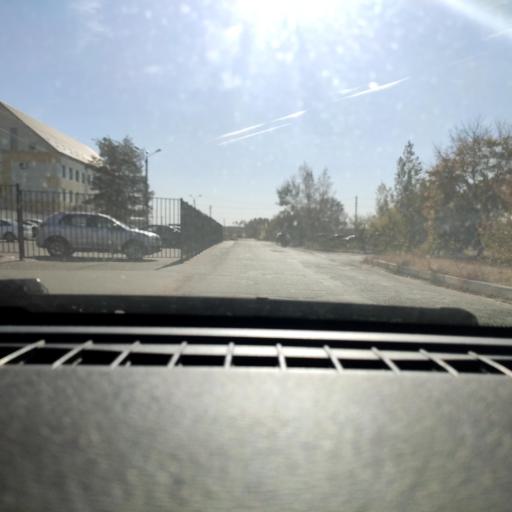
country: RU
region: Voronezj
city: Maslovka
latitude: 51.5923
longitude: 39.2370
